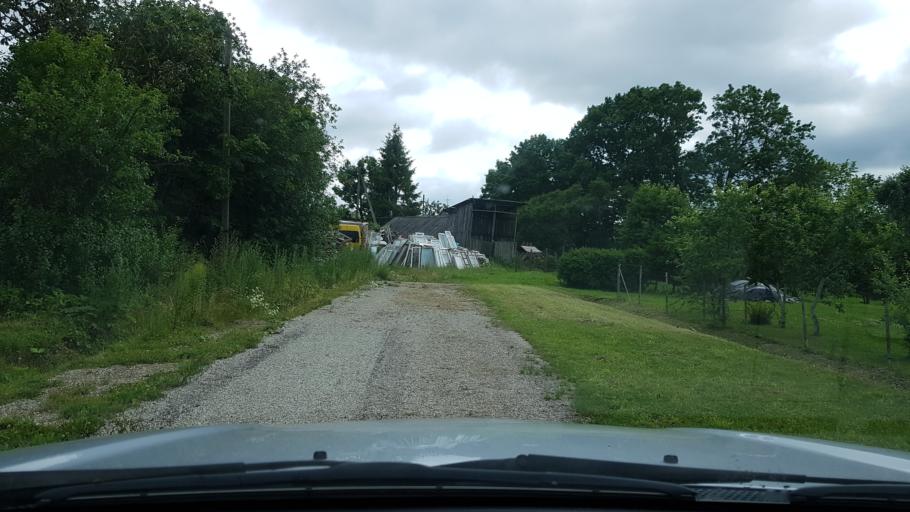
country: EE
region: Ida-Virumaa
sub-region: Narva linn
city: Narva
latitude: 59.3961
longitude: 28.1260
